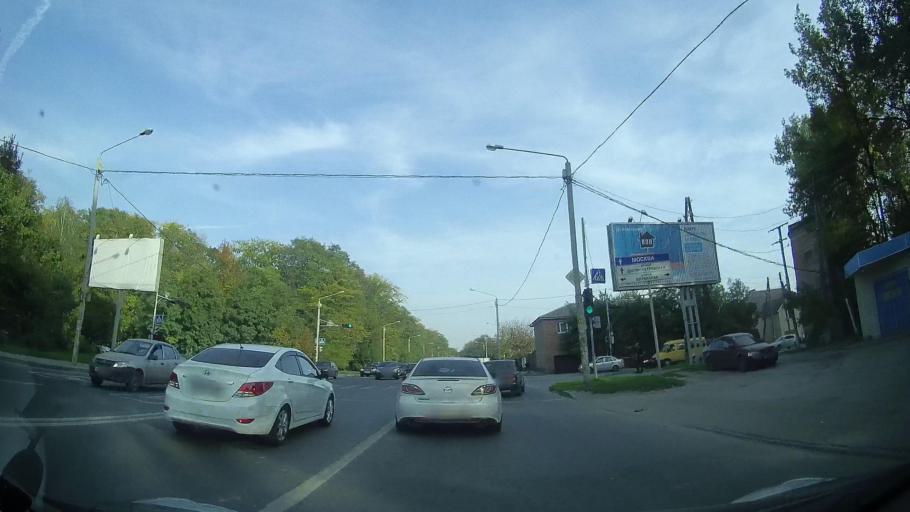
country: RU
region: Rostov
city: Imeni Chkalova
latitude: 47.2772
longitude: 39.7826
